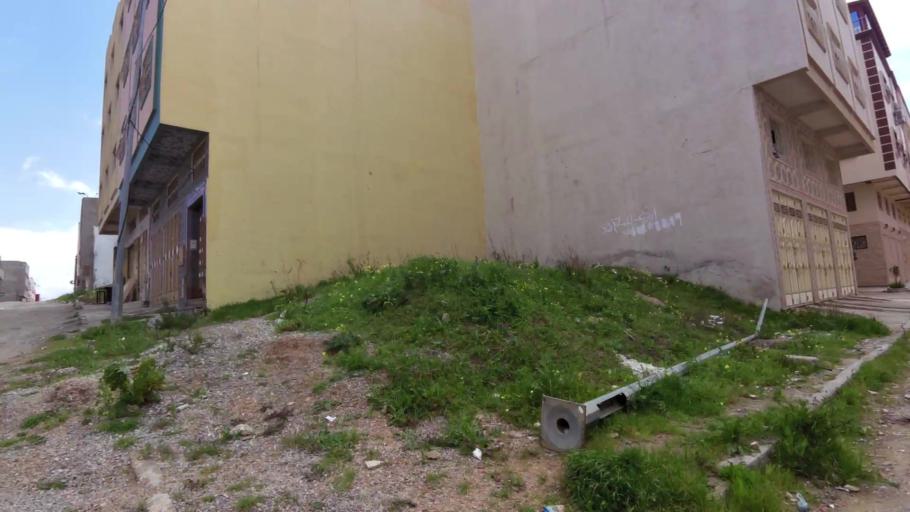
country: MA
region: Tanger-Tetouan
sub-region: Tanger-Assilah
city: Tangier
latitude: 35.7599
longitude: -5.8511
